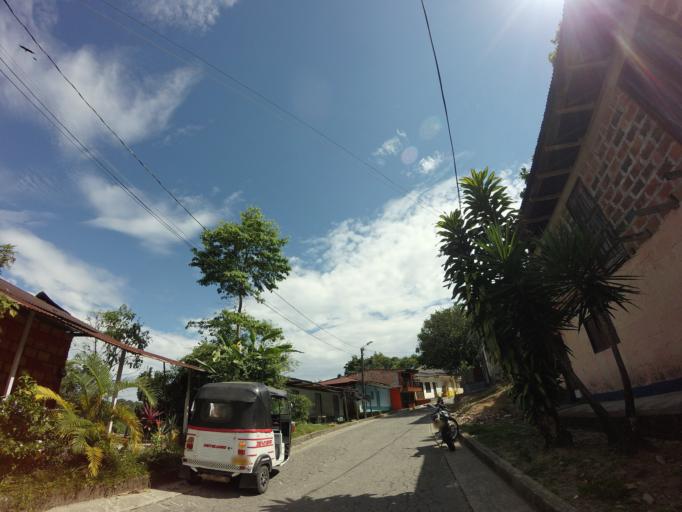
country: CO
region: Caldas
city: Norcasia
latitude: 5.5742
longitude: -74.8913
